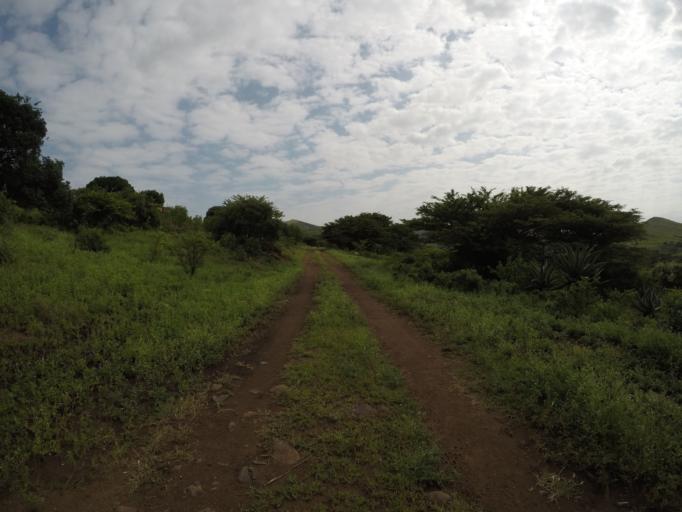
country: ZA
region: KwaZulu-Natal
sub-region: uThungulu District Municipality
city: Empangeni
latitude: -28.6277
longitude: 31.9099
